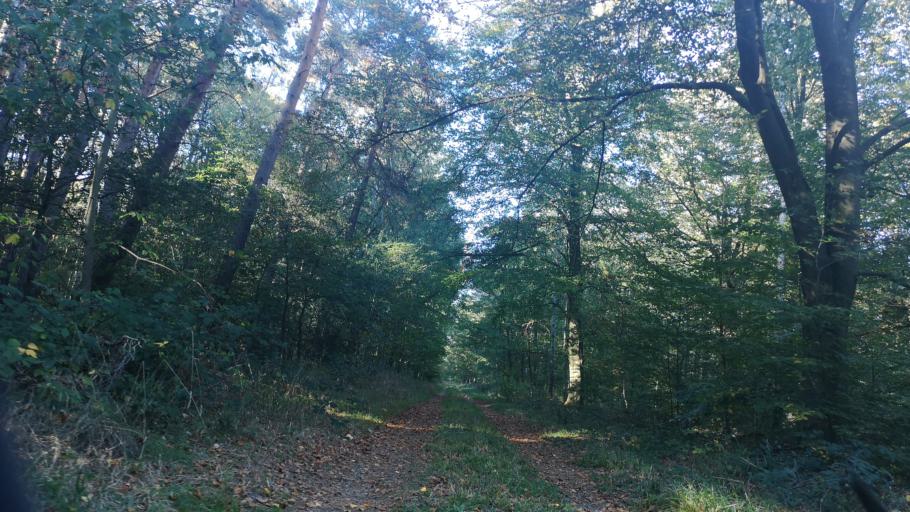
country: DE
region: North Rhine-Westphalia
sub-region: Regierungsbezirk Koln
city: Kreuzau
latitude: 50.7454
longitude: 6.5166
